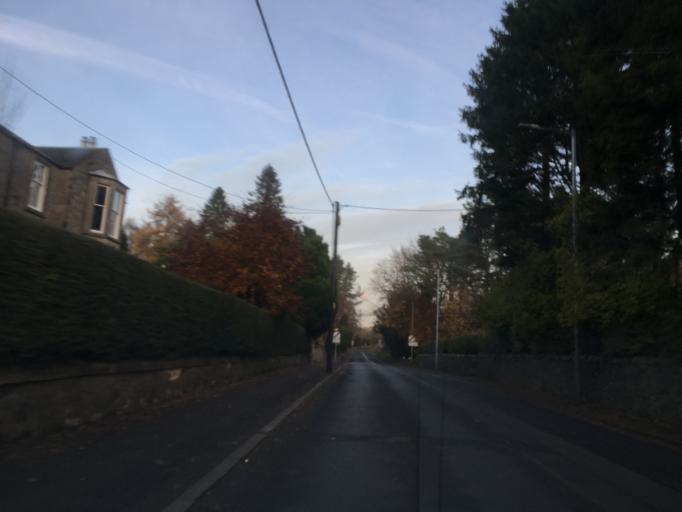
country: GB
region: Scotland
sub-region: Clackmannanshire
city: Dollar
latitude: 56.1635
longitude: -3.6672
